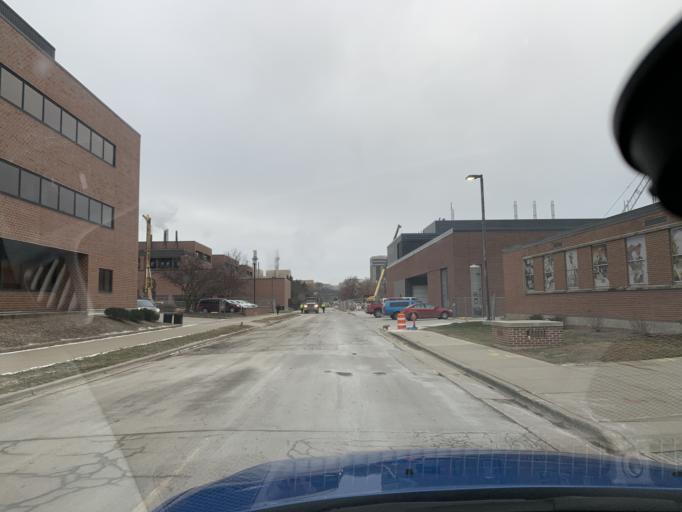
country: US
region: Wisconsin
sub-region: Dane County
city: Madison
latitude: 43.0756
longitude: -89.4179
